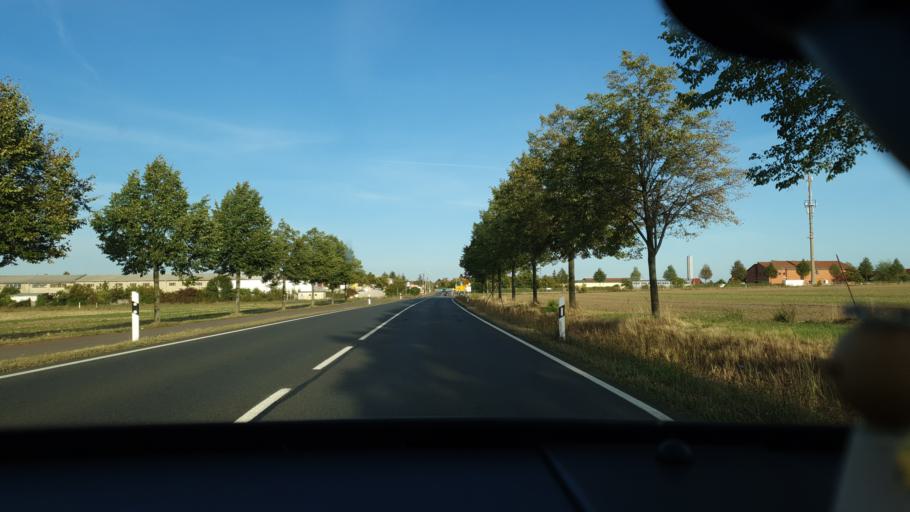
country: DE
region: Saxony
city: Eilenburg
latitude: 51.4589
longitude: 12.6047
